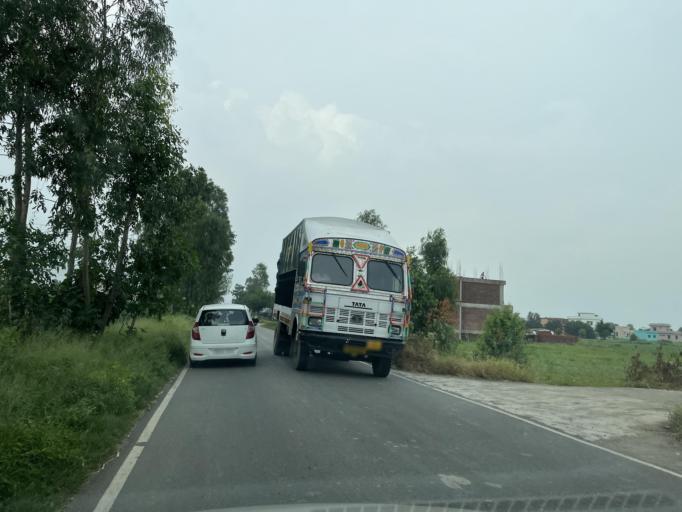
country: IN
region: Uttarakhand
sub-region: Naini Tal
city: Haldwani
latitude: 29.1823
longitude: 79.4744
